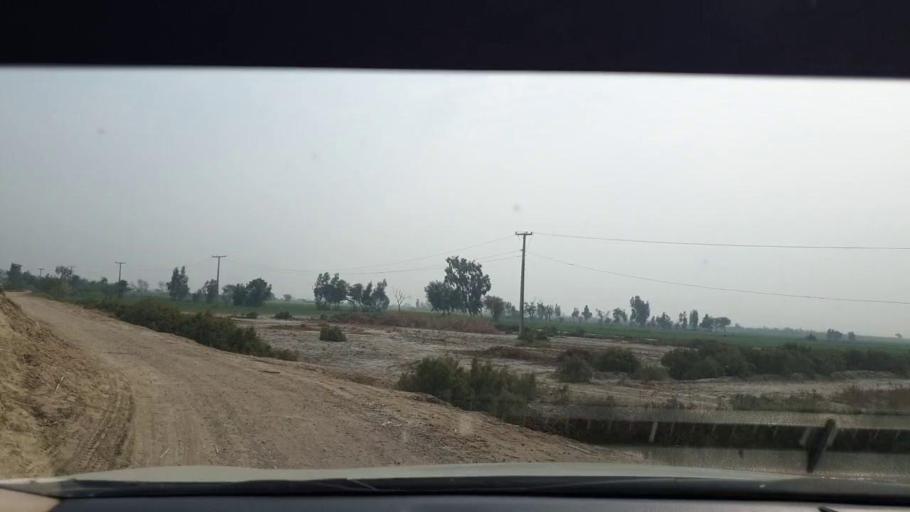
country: PK
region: Sindh
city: Berani
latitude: 25.8330
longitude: 68.8278
